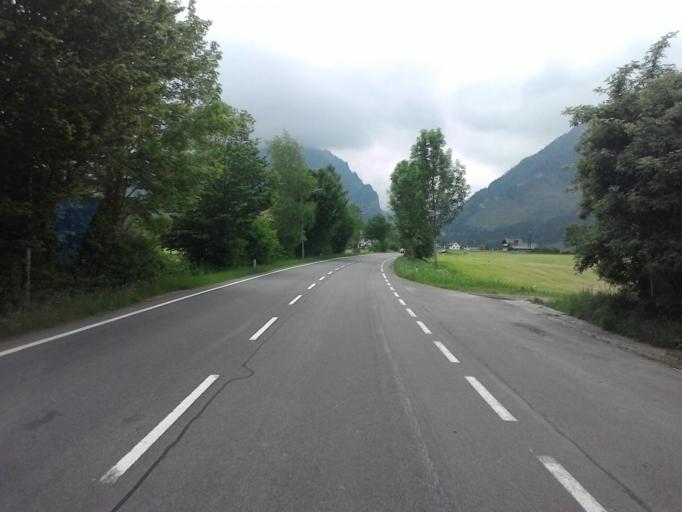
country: AT
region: Styria
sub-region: Politischer Bezirk Liezen
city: Gams bei Hieflau
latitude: 47.6513
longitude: 14.7635
